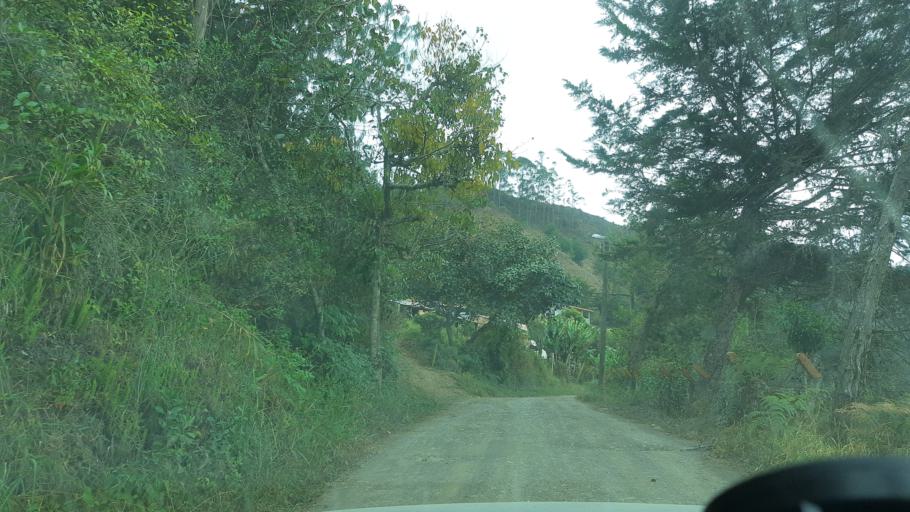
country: CO
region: Boyaca
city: Somondoco
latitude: 4.9727
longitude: -73.3797
